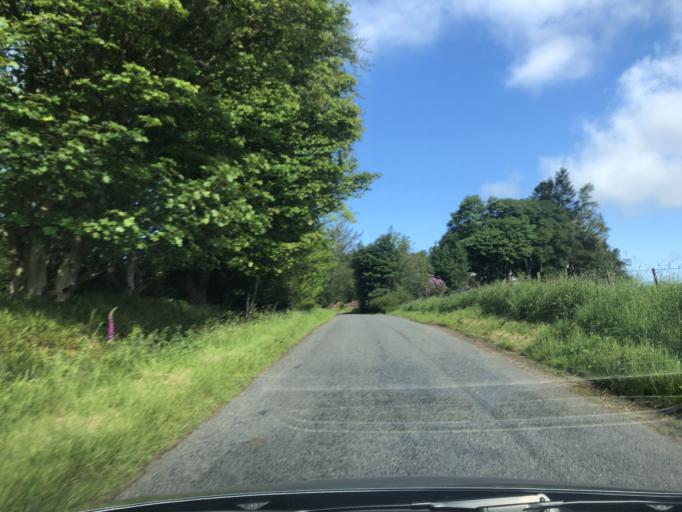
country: GB
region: Scotland
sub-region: Angus
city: Kirriemuir
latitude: 56.7324
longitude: -3.0091
